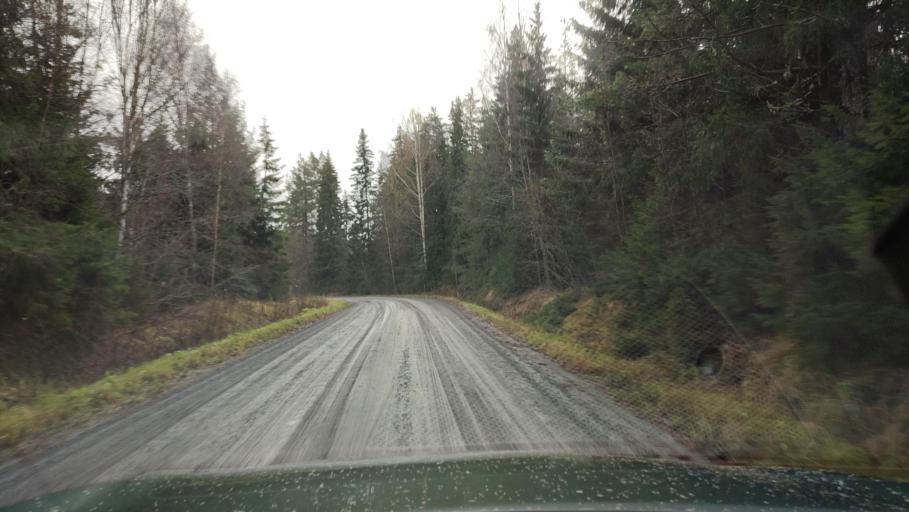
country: FI
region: Ostrobothnia
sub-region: Sydosterbotten
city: Naerpes
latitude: 62.4626
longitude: 21.4895
